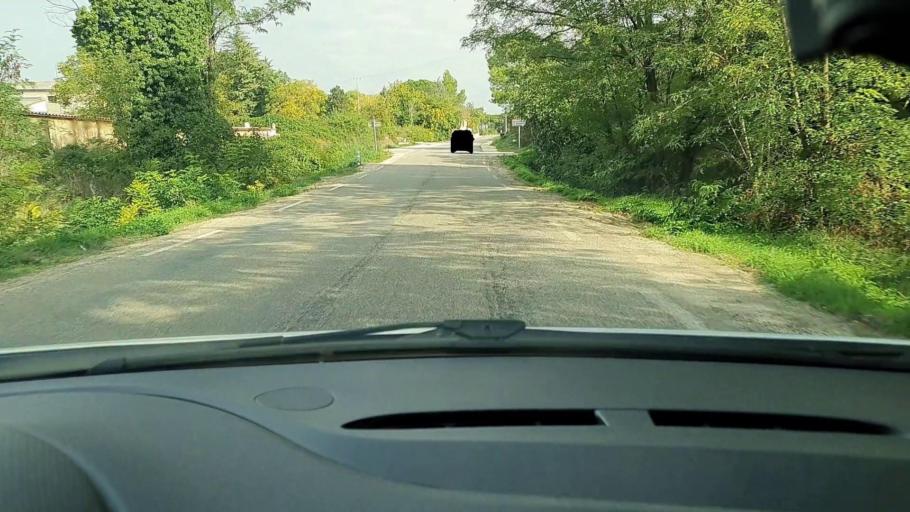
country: FR
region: Languedoc-Roussillon
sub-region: Departement du Gard
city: Saint-Quentin-la-Poterie
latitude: 44.1008
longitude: 4.4546
